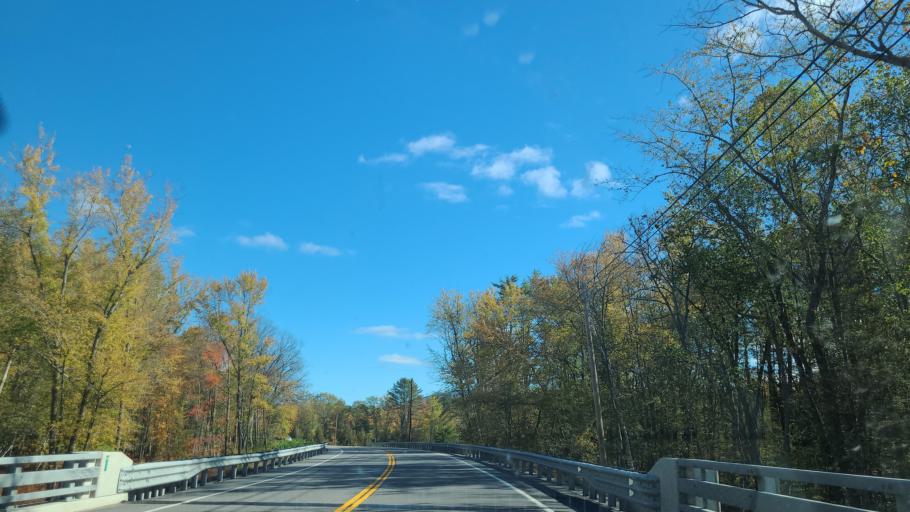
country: US
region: Maine
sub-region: Oxford County
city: Fryeburg
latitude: 44.0295
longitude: -70.9047
